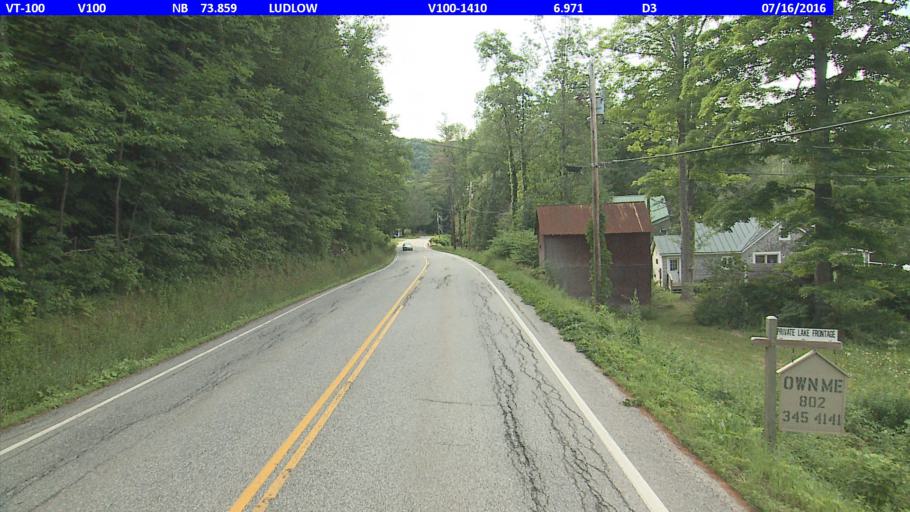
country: US
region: Vermont
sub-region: Windsor County
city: Chester
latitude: 43.4448
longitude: -72.7024
